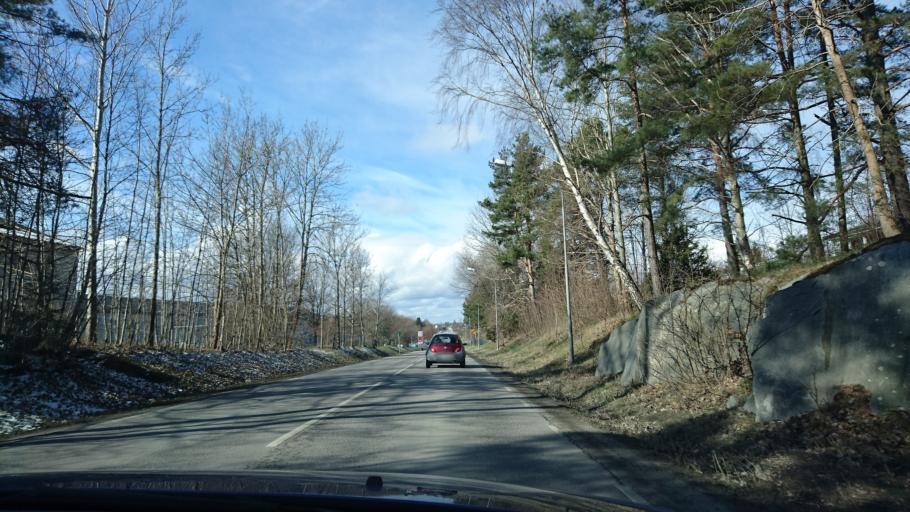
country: SE
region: Stockholm
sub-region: Norrtalje Kommun
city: Norrtalje
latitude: 59.7695
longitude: 18.7246
